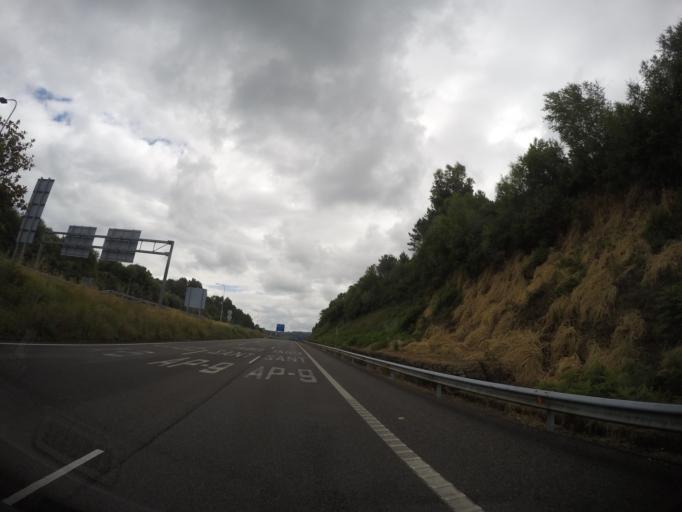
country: ES
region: Galicia
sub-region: Provincia da Coruna
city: Bergondo
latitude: 43.2819
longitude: -8.2723
